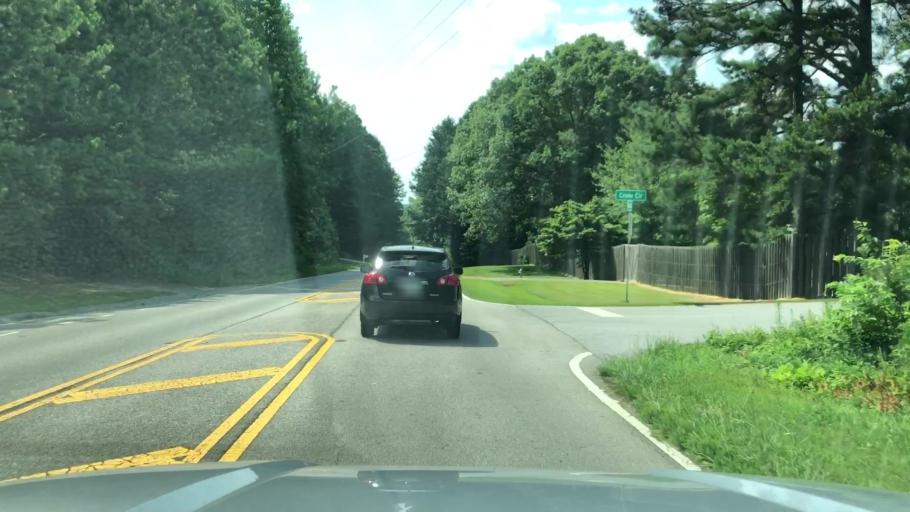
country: US
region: Georgia
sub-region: Paulding County
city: Hiram
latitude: 33.9471
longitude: -84.7700
